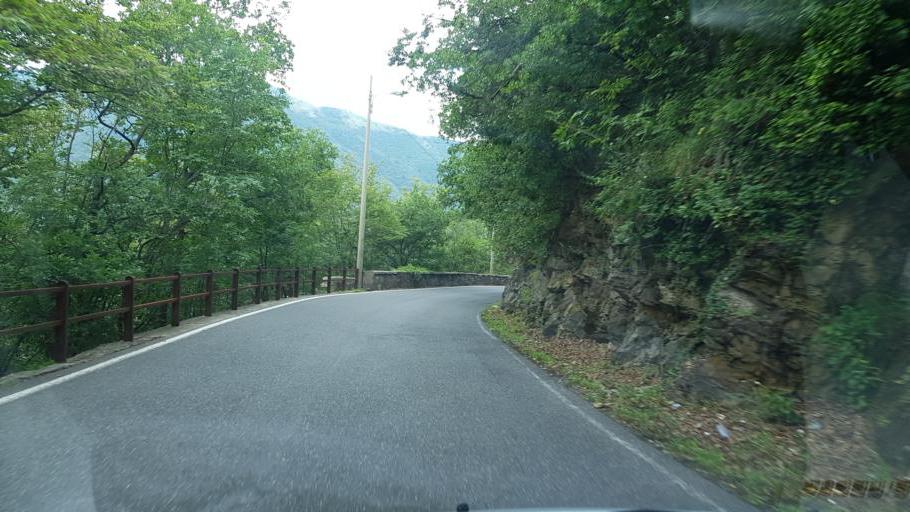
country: IT
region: Liguria
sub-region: Provincia di Genova
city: Piccarello
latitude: 44.4259
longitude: 9.0080
